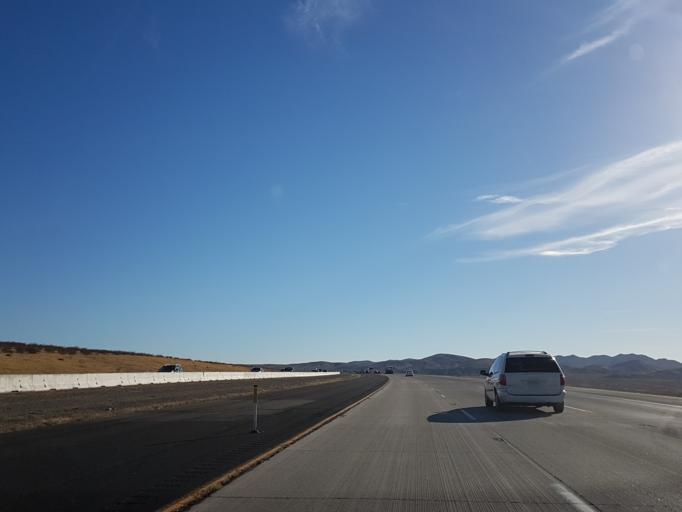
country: US
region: California
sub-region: San Bernardino County
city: Lenwood
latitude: 34.7237
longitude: -117.1933
